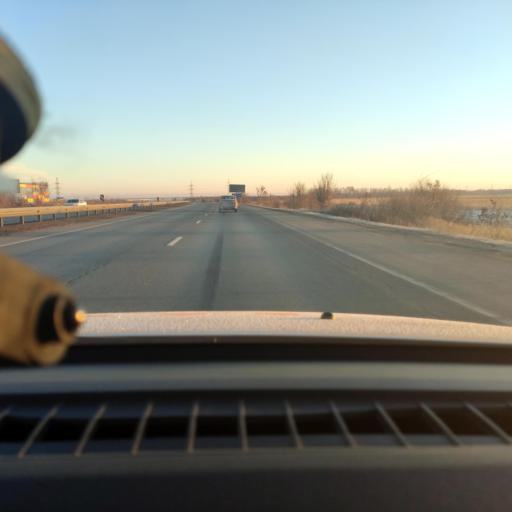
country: RU
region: Samara
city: Novokuybyshevsk
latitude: 53.0055
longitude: 49.9680
